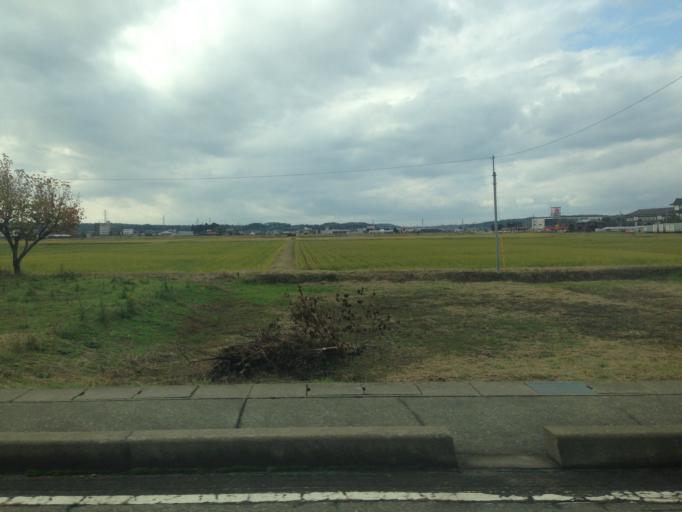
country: JP
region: Ishikawa
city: Komatsu
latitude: 36.3063
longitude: 136.3698
